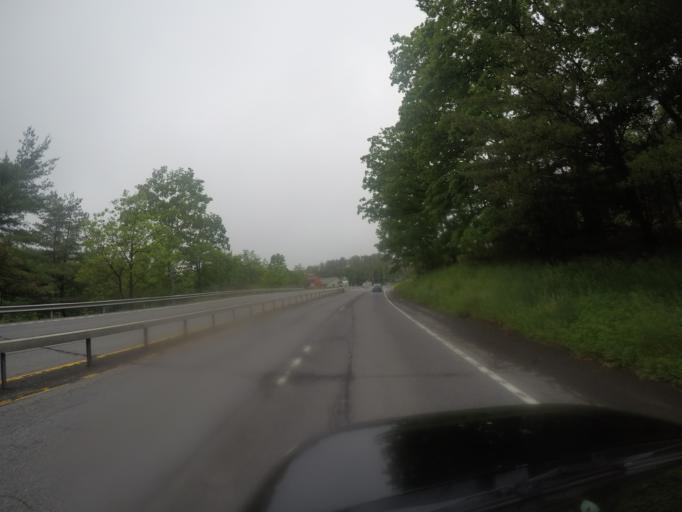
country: US
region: New York
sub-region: Ulster County
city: West Hurley
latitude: 41.9725
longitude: -74.0779
